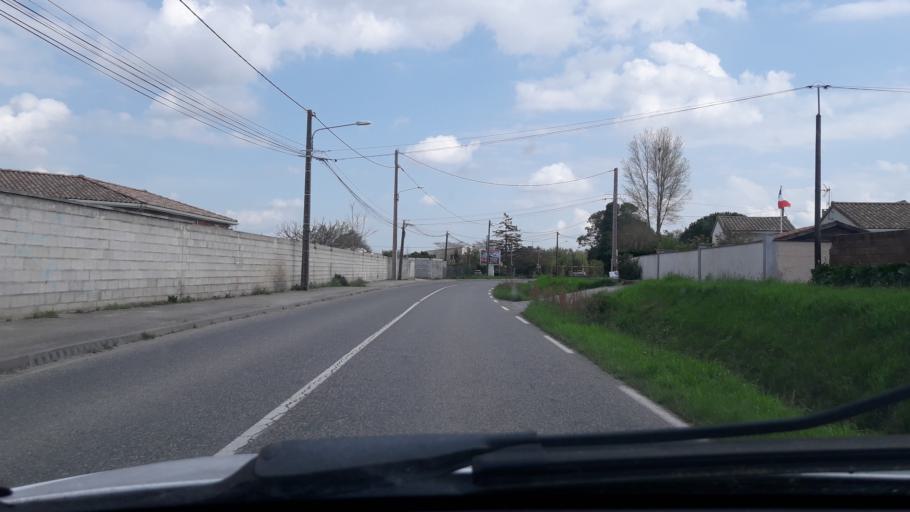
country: FR
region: Midi-Pyrenees
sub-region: Departement de la Haute-Garonne
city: Seysses
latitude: 43.4977
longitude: 1.2980
